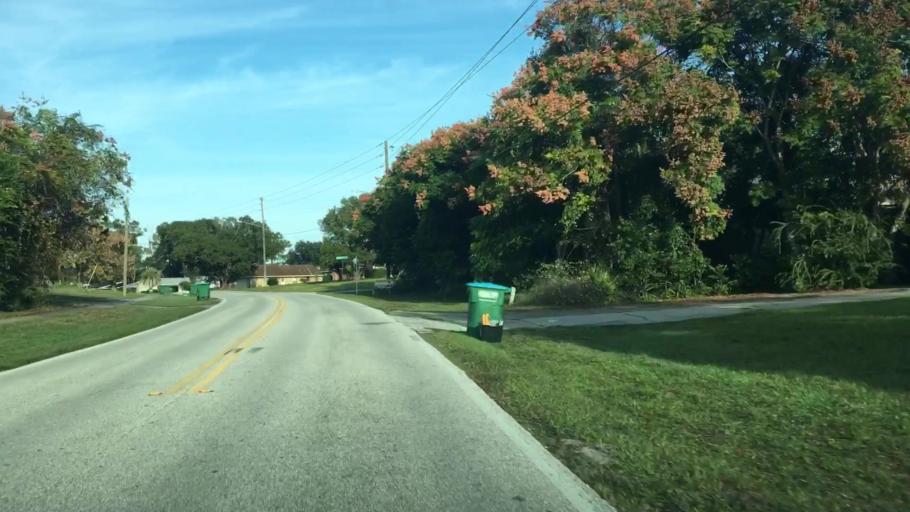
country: US
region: Florida
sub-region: Volusia County
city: Deltona
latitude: 28.9217
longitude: -81.2387
